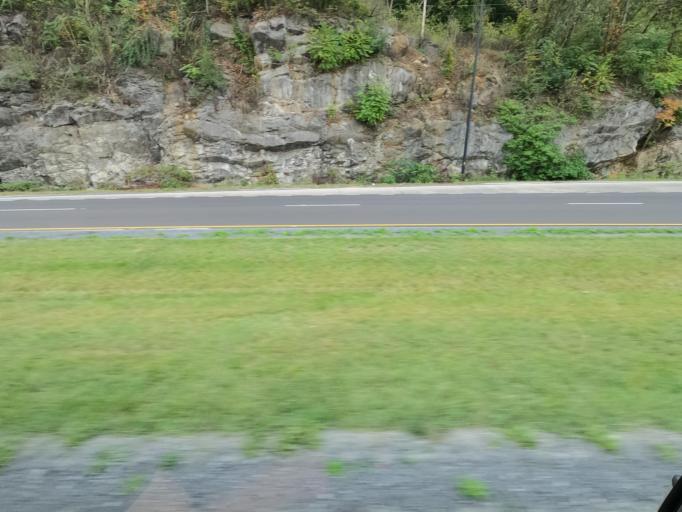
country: US
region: Tennessee
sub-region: Sullivan County
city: Colonial Heights
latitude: 36.5190
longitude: -82.5168
